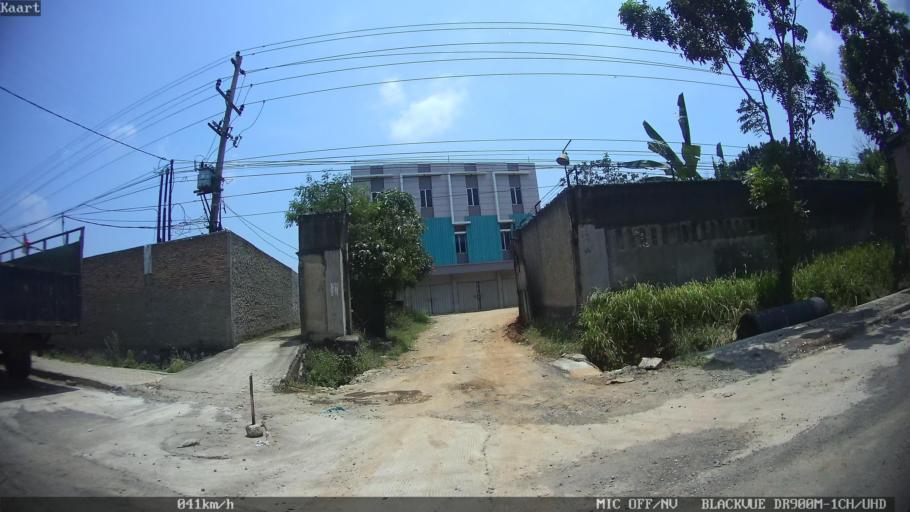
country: ID
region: Lampung
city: Kedaton
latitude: -5.3629
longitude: 105.2594
